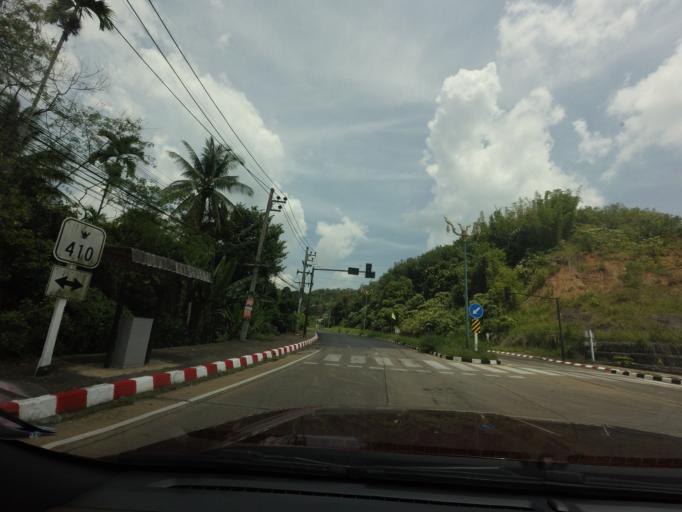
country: TH
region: Yala
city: Betong
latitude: 5.7679
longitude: 101.0521
